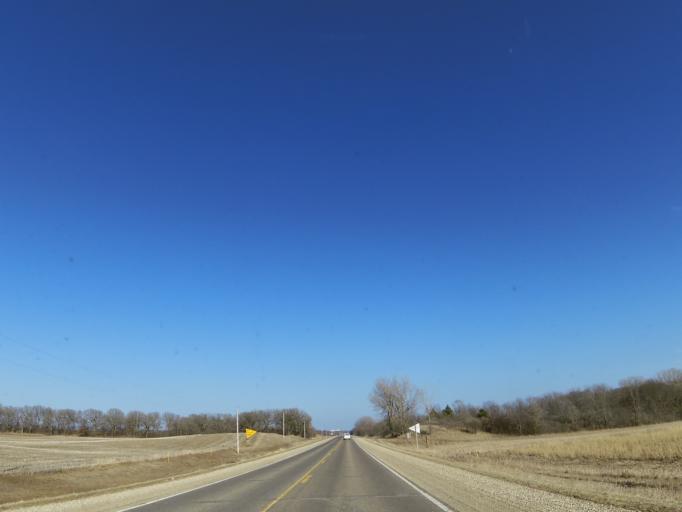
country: US
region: Iowa
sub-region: Worth County
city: Northwood
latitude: 43.4443
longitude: -93.2692
